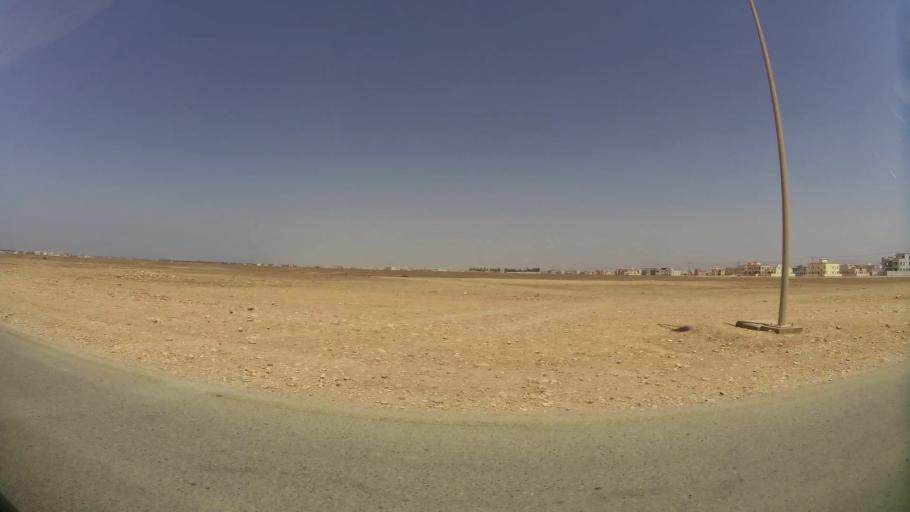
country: OM
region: Zufar
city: Salalah
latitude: 17.0670
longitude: 54.2105
